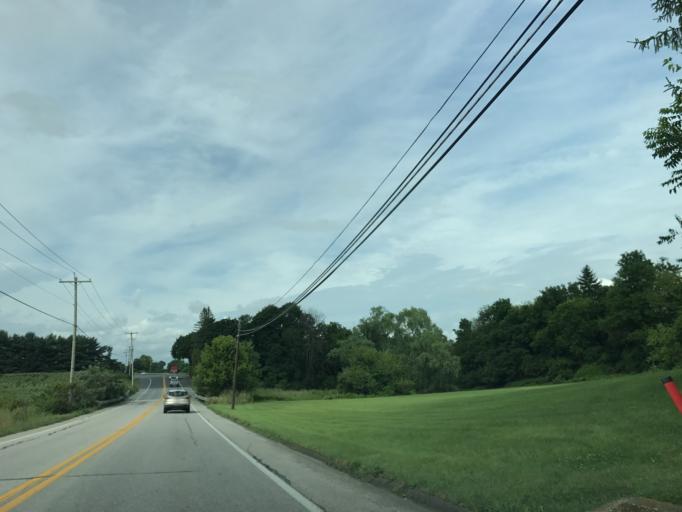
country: US
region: Pennsylvania
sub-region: York County
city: Weigelstown
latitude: 39.9244
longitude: -76.8257
